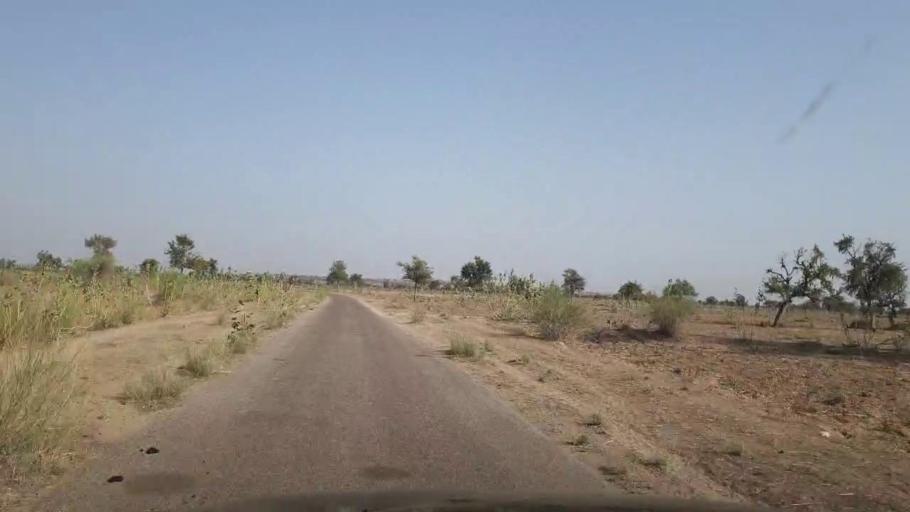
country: PK
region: Sindh
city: Islamkot
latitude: 25.1325
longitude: 70.4740
